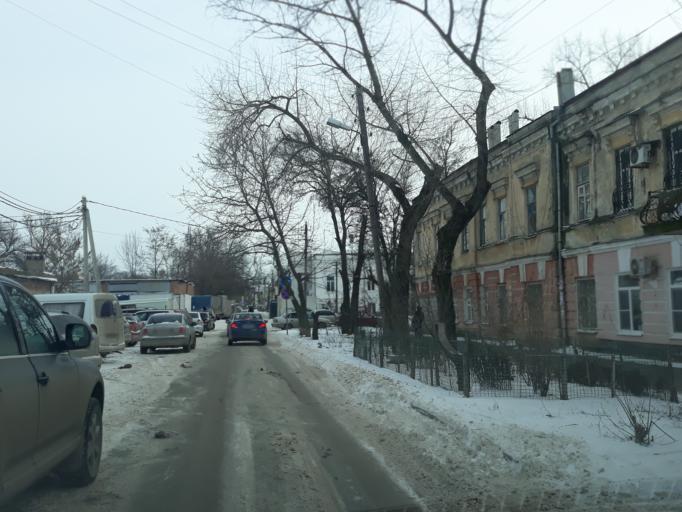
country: RU
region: Rostov
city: Taganrog
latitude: 47.2110
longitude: 38.9171
